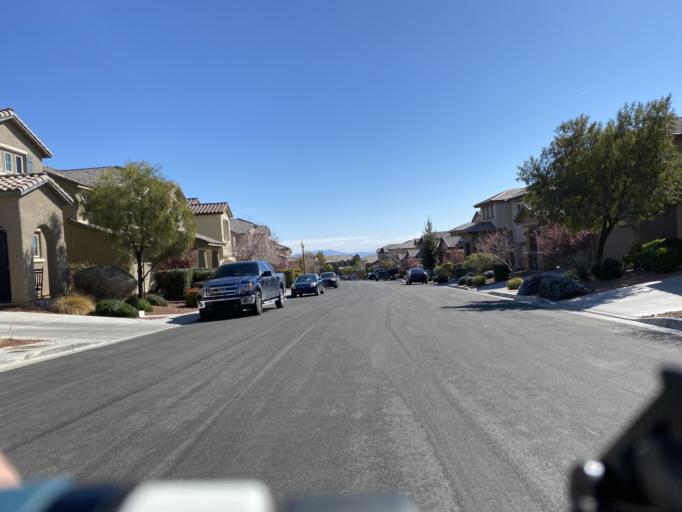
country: US
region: Nevada
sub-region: Clark County
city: Summerlin South
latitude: 36.2909
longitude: -115.3223
